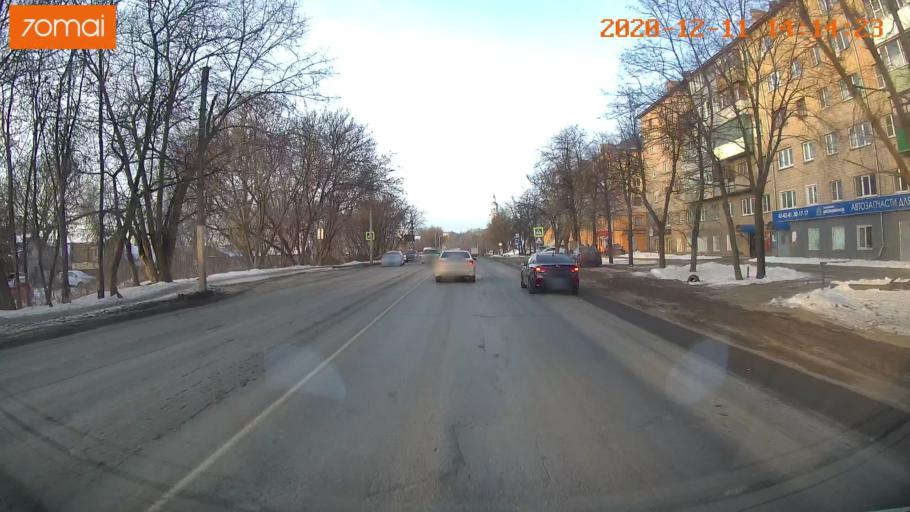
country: RU
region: Kostroma
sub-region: Kostromskoy Rayon
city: Kostroma
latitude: 57.7523
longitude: 40.9518
